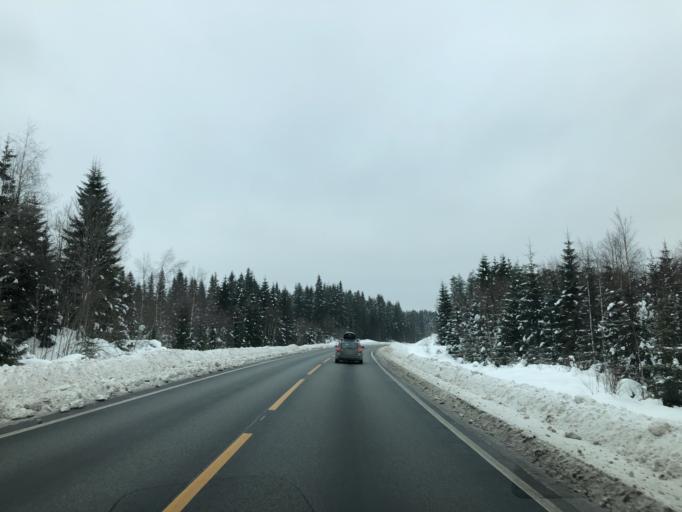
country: NO
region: Hedmark
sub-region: Elverum
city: Elverum
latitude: 60.9377
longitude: 11.6790
